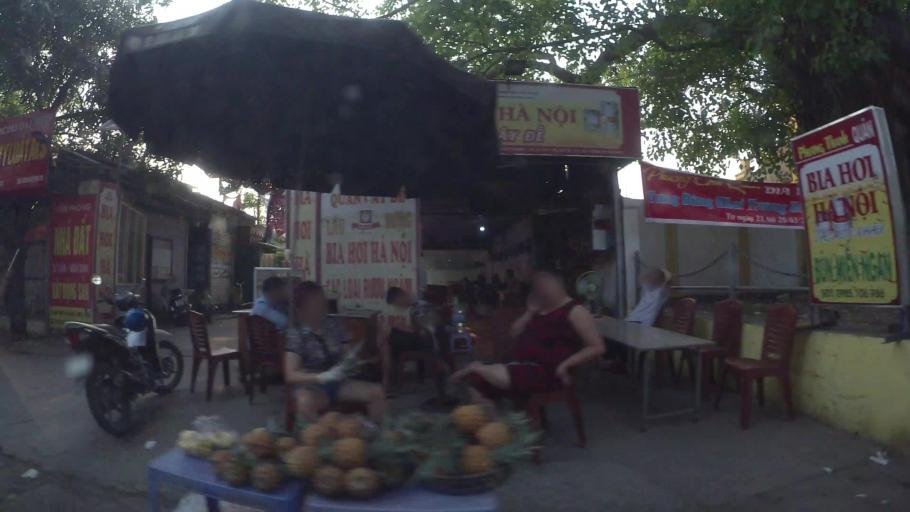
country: VN
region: Ha Noi
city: Van Dien
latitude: 20.9384
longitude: 105.8396
